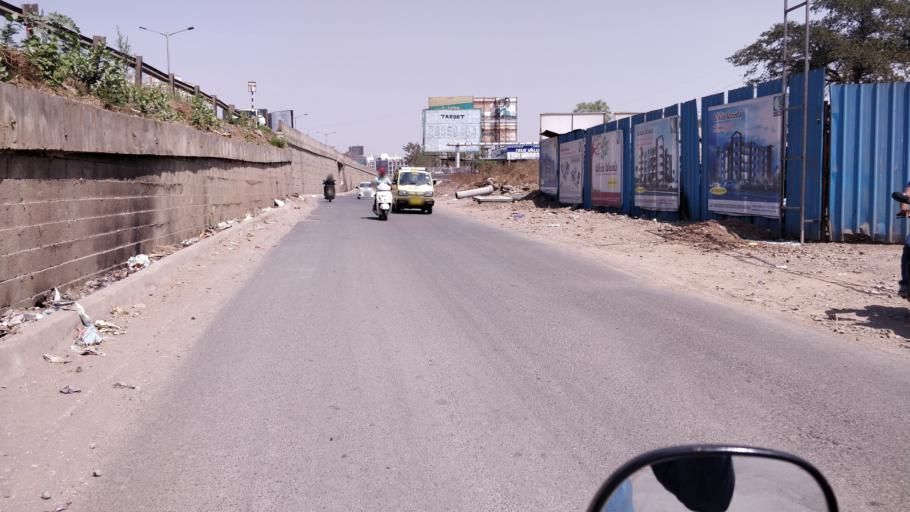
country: IN
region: Maharashtra
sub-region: Pune Division
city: Kharakvasla
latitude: 18.5148
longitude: 73.7694
